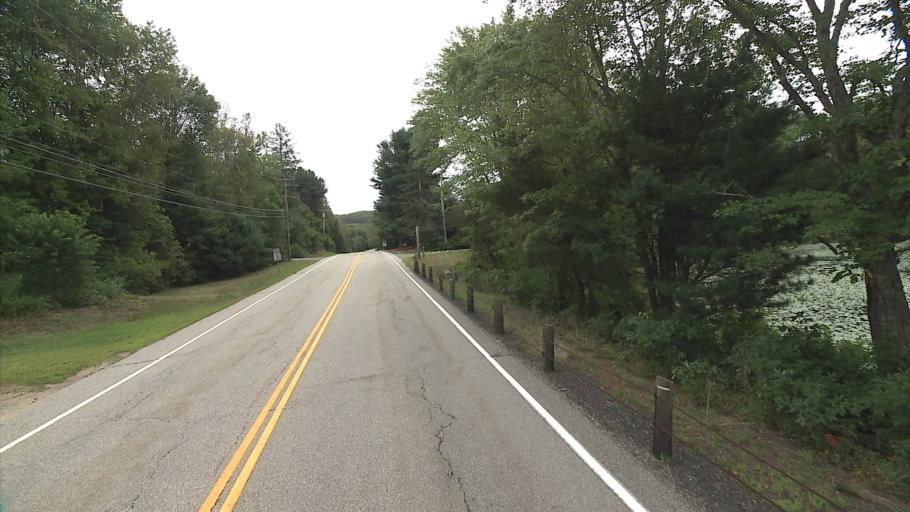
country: US
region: Connecticut
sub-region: Middlesex County
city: Essex Village
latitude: 41.4336
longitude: -72.3387
